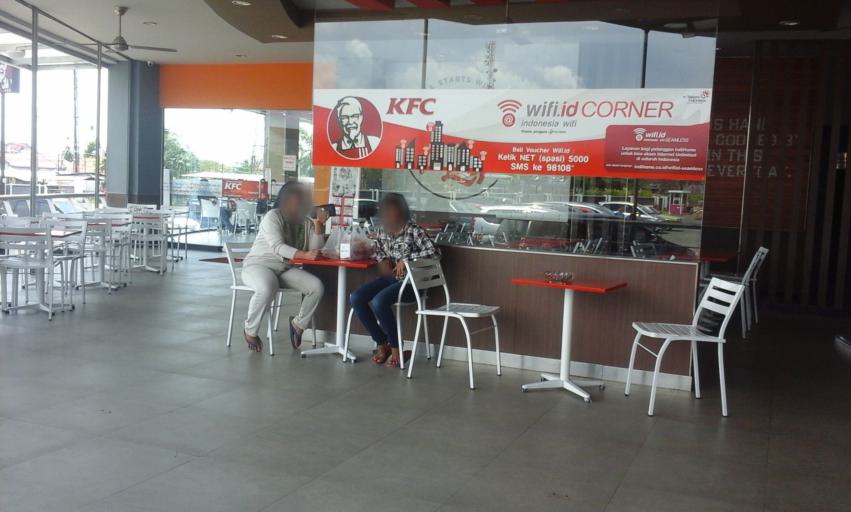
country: ID
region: East Java
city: Krajan
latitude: -8.1847
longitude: 113.6630
